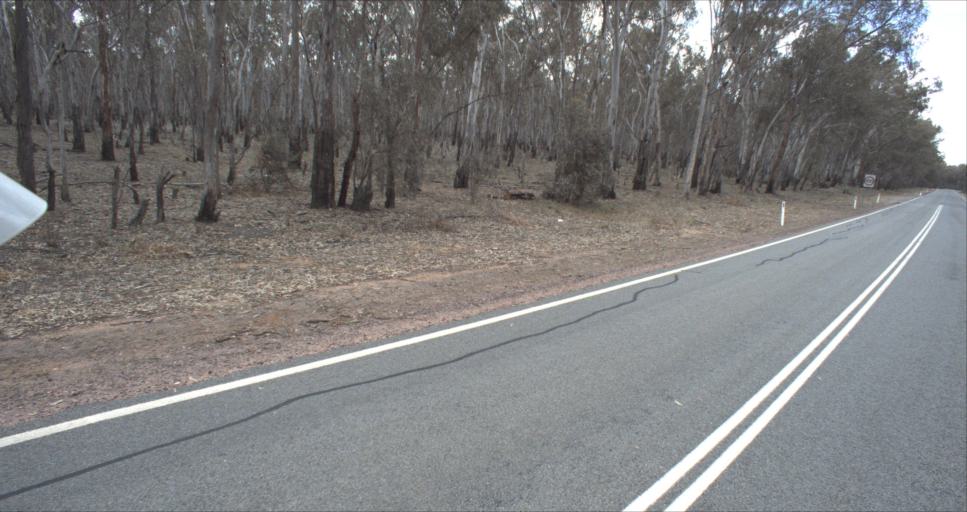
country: AU
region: New South Wales
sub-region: Leeton
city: Leeton
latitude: -34.6298
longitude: 146.3765
